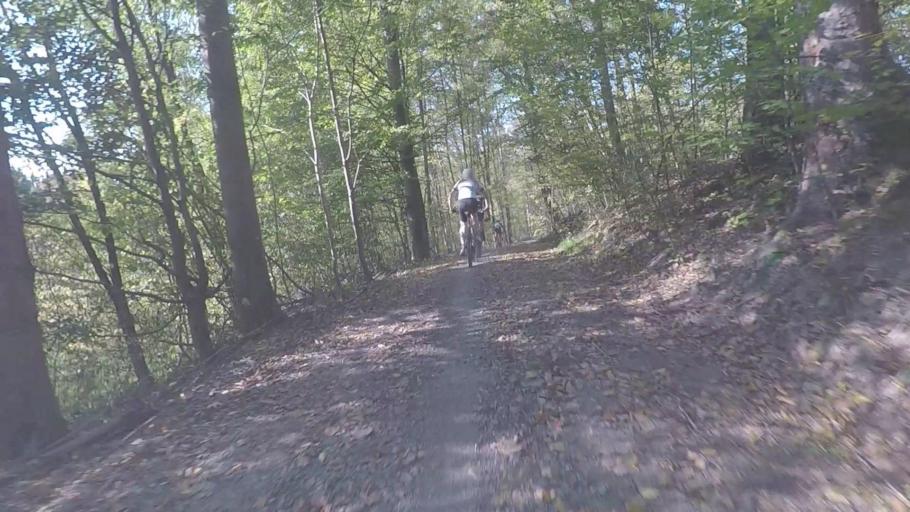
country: DE
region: Baden-Wuerttemberg
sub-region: Regierungsbezirk Stuttgart
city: Spiegelberg
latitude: 49.0345
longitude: 9.4531
